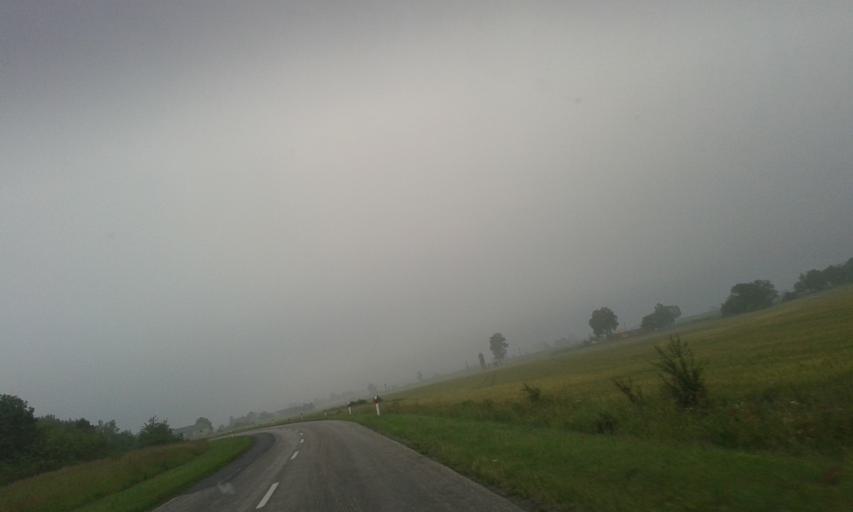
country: PL
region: Pomeranian Voivodeship
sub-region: Powiat czluchowski
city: Debrzno
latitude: 53.5195
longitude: 17.2335
